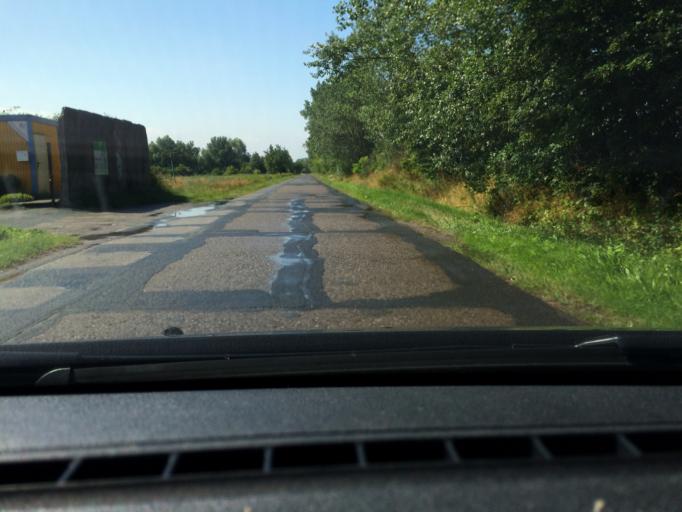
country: DE
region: Mecklenburg-Vorpommern
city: Altenpleen
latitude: 54.3650
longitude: 12.9090
